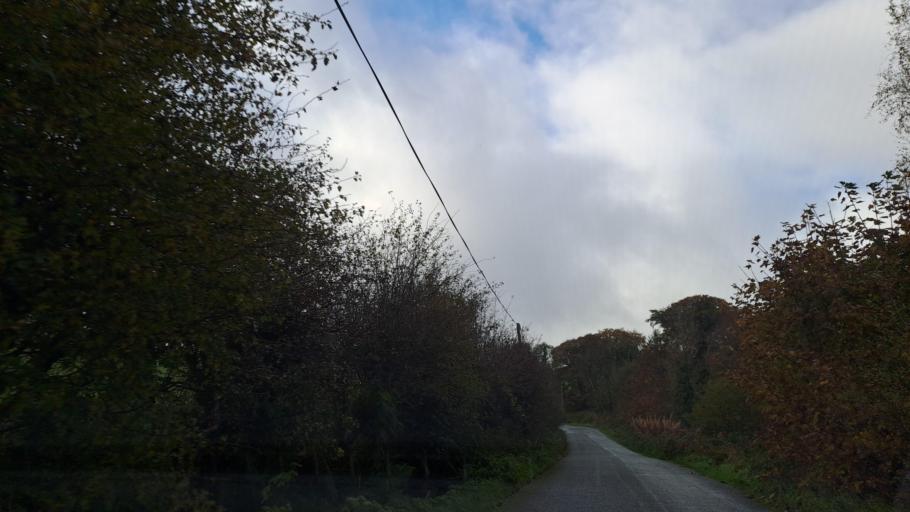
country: IE
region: Ulster
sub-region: An Cabhan
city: Bailieborough
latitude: 53.9588
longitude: -6.9875
